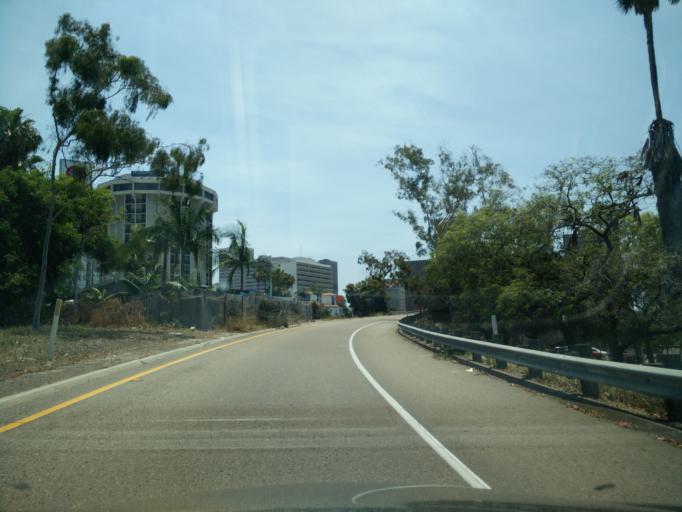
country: US
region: California
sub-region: San Diego County
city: San Diego
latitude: 32.7233
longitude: -117.1647
